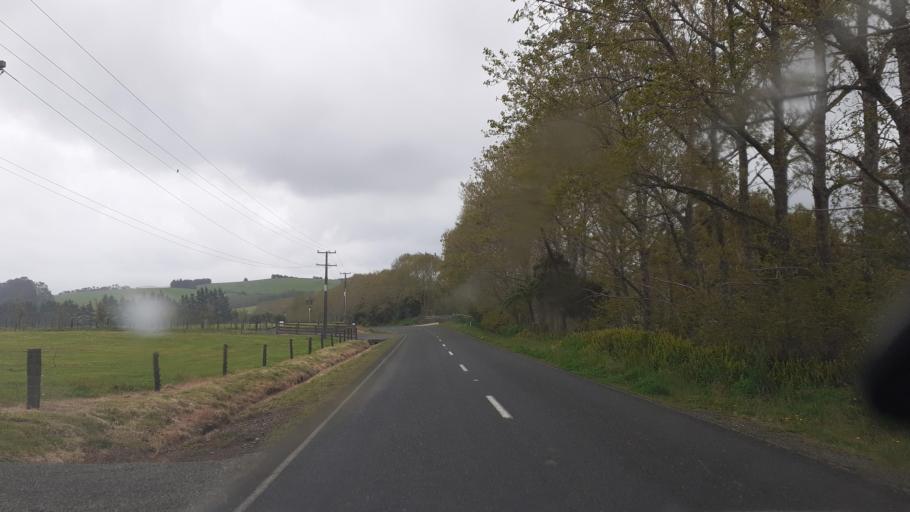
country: NZ
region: Northland
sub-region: Far North District
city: Waimate North
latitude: -35.2740
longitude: 173.8284
